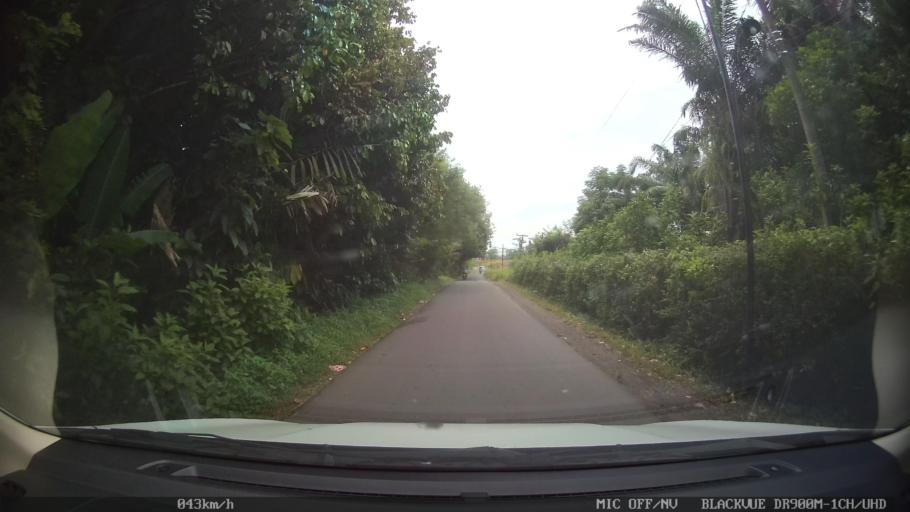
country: ID
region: North Sumatra
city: Sunggal
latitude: 3.5727
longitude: 98.5780
